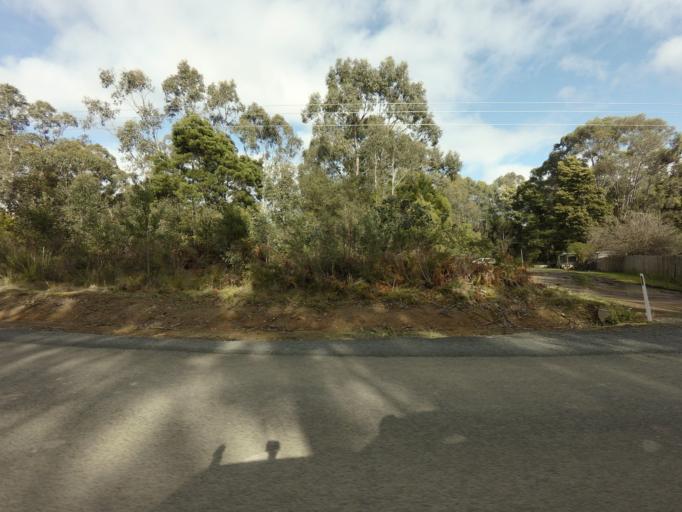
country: AU
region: Tasmania
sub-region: Huon Valley
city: Geeveston
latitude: -43.4452
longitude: 146.9045
